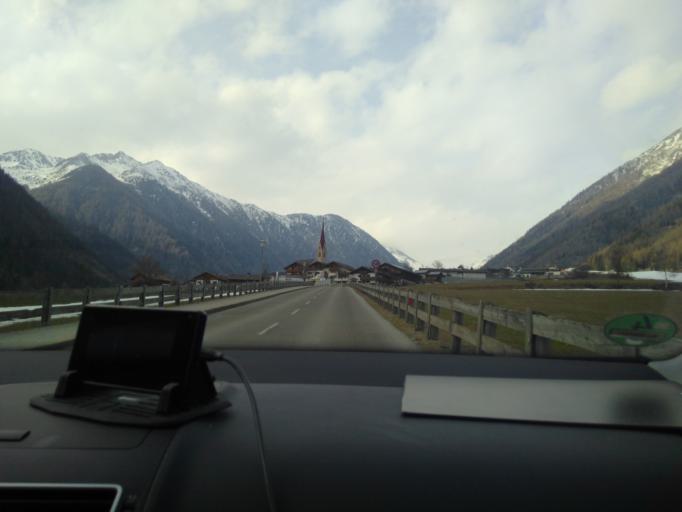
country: IT
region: Trentino-Alto Adige
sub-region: Bolzano
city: Fortezza
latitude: 46.8363
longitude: 11.6288
